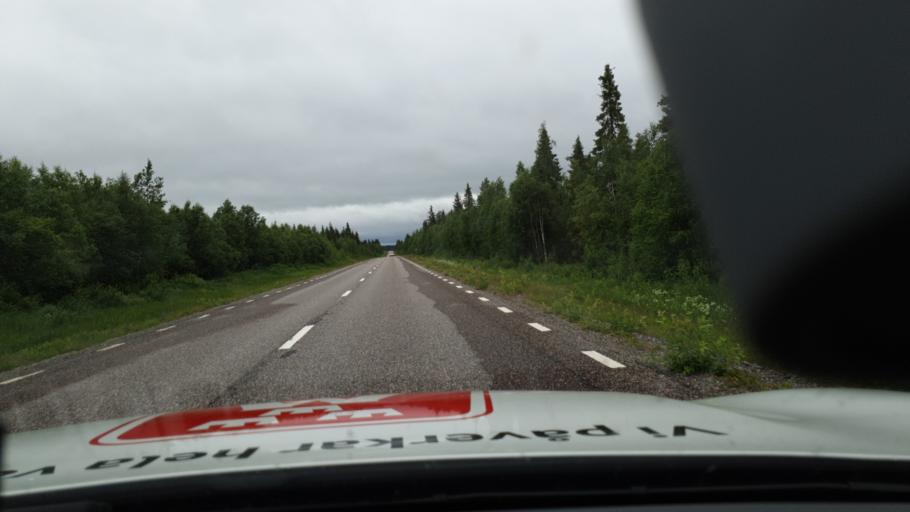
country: SE
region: Norrbotten
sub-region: Pajala Kommun
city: Pajala
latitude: 67.1390
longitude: 23.5767
